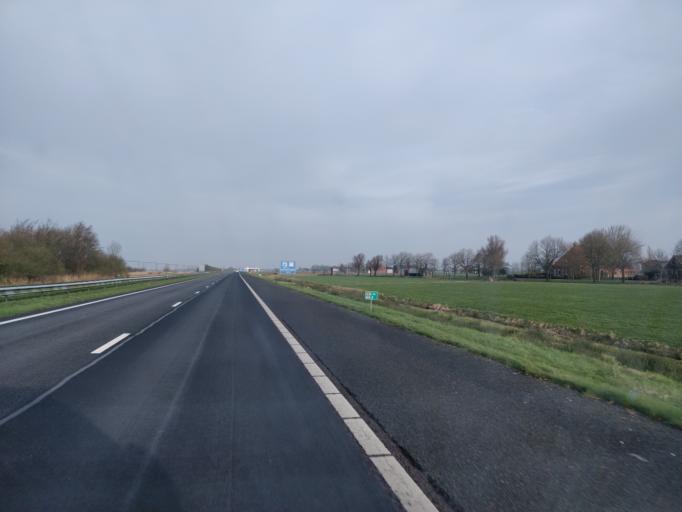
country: NL
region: Friesland
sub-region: Gemeente Boarnsterhim
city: Reduzum
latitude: 53.1203
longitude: 5.8085
